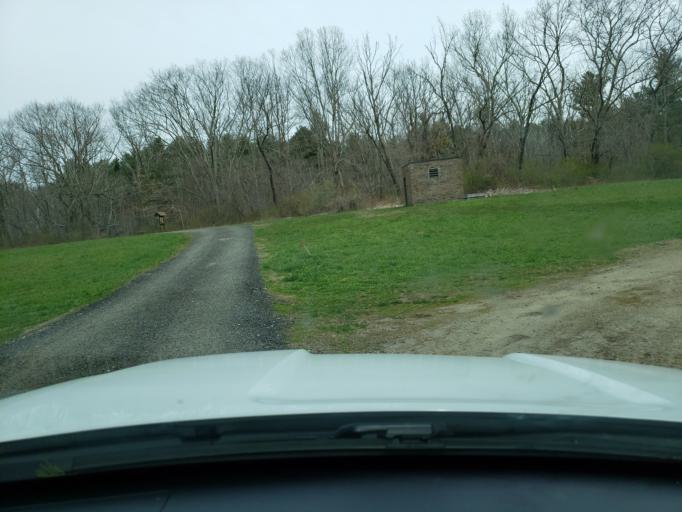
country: US
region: Connecticut
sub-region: Windham County
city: Wauregan
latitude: 41.7347
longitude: -71.9189
